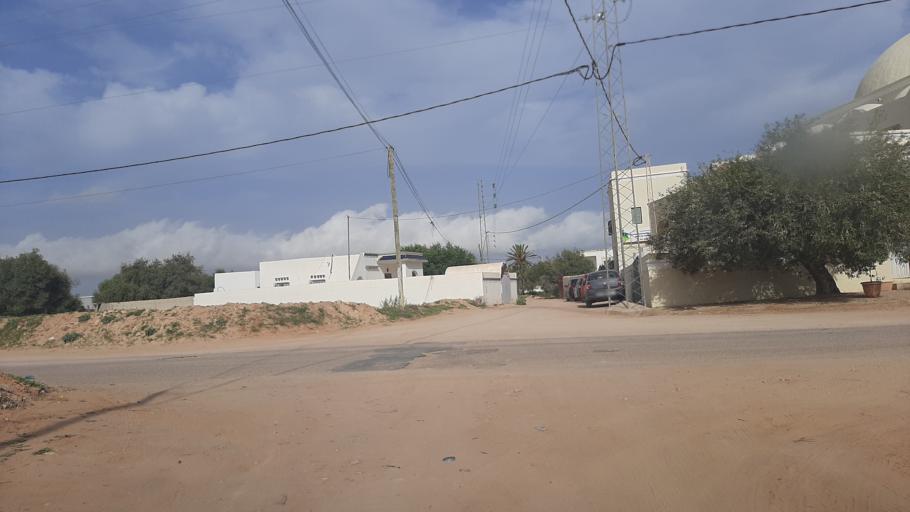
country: TN
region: Madanin
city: Midoun
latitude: 33.7980
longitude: 11.0288
